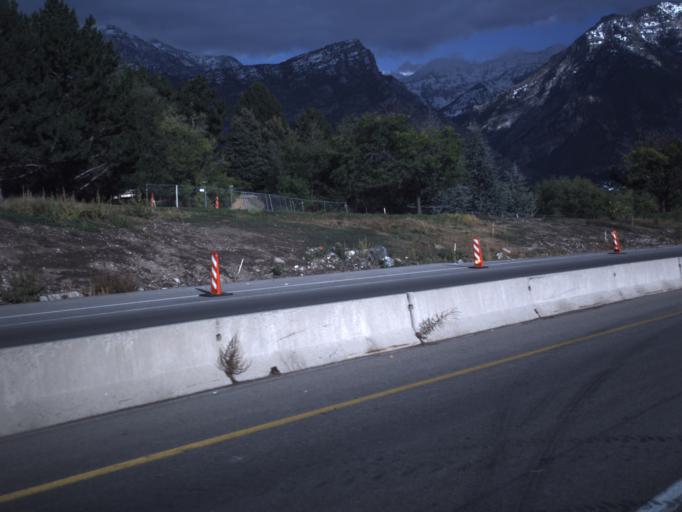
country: US
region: Utah
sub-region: Utah County
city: Orem
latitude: 40.2724
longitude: -111.6736
